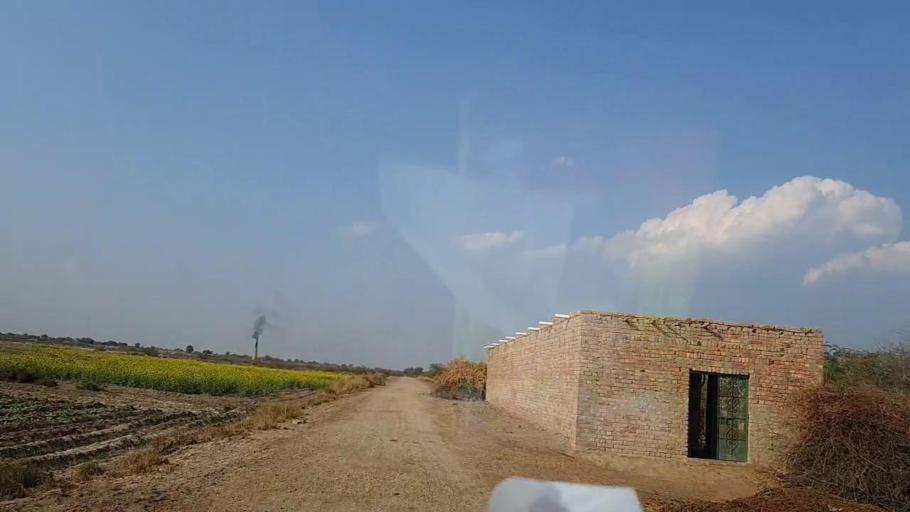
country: PK
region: Sindh
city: Nawabshah
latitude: 26.1612
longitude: 68.4136
